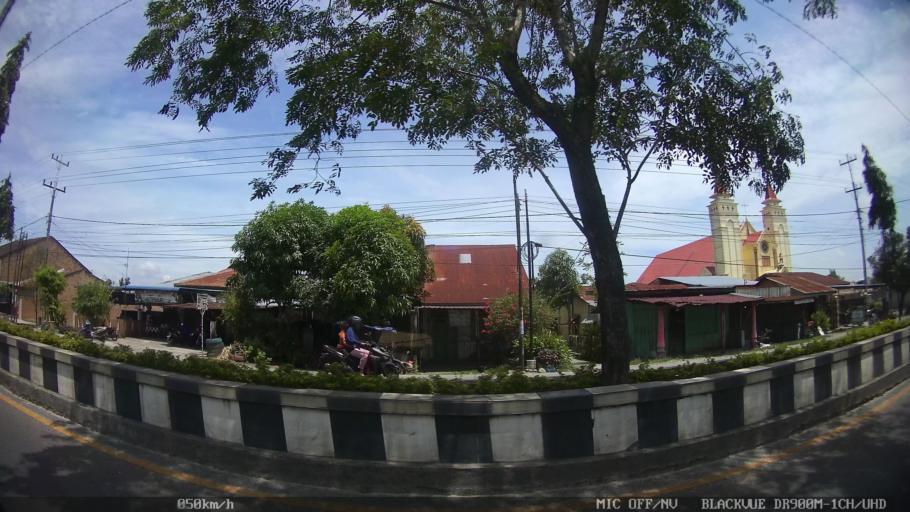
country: ID
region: North Sumatra
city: Percut
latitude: 3.5553
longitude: 98.8824
